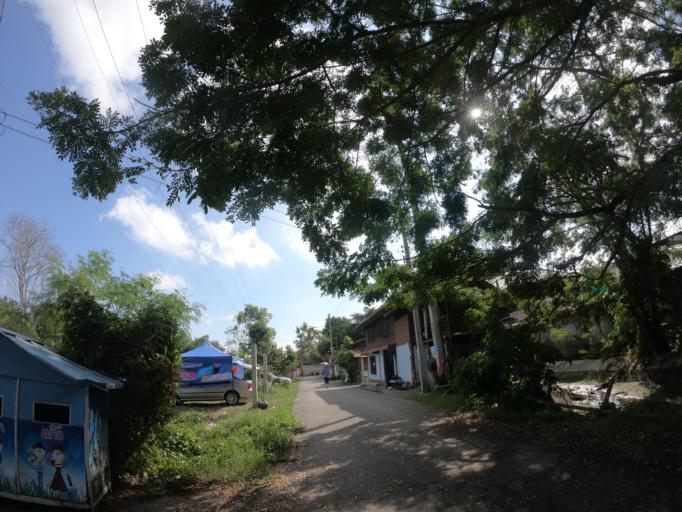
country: TH
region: Chiang Mai
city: Chiang Mai
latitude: 18.7878
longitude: 99.0374
